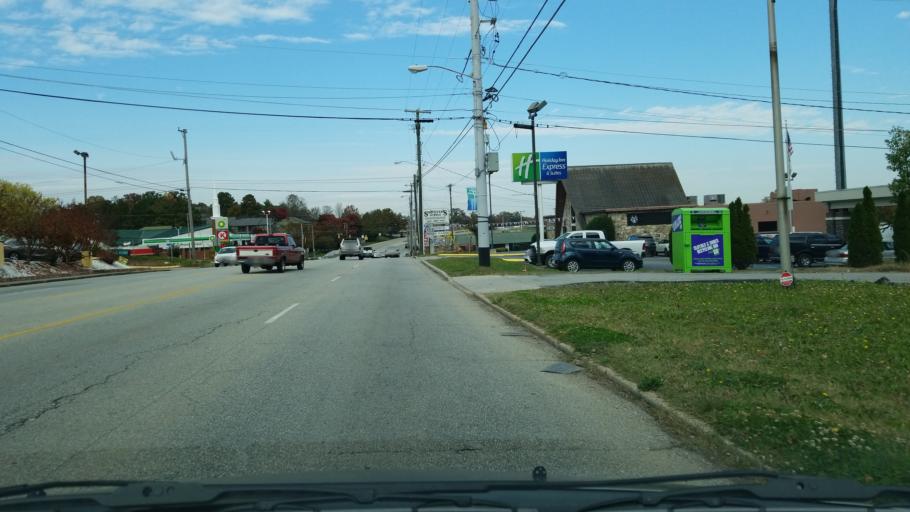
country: US
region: Tennessee
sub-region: Hamilton County
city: Red Bank
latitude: 35.1269
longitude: -85.2469
